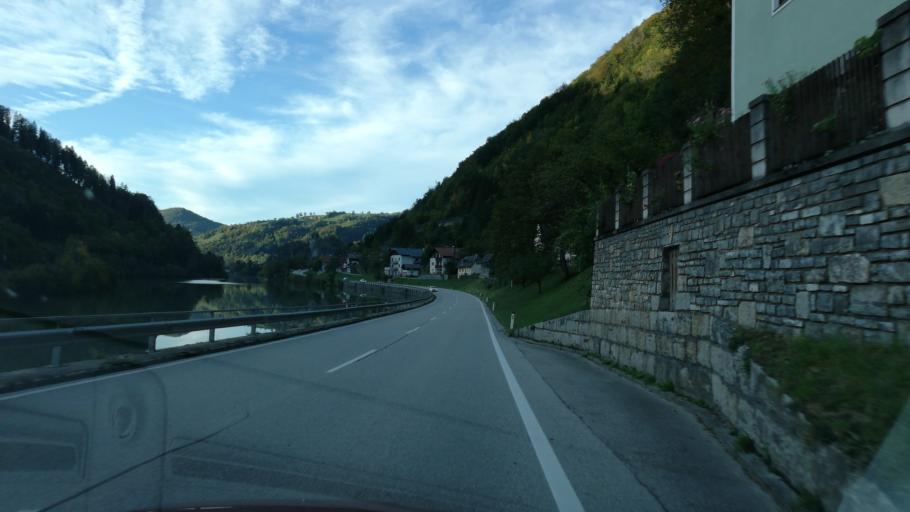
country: AT
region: Upper Austria
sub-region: Politischer Bezirk Steyr-Land
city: Losenstein
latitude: 47.9114
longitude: 14.4501
